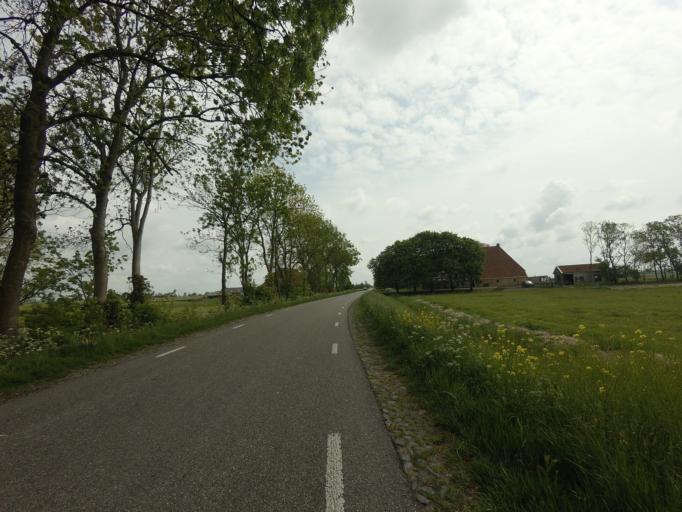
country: NL
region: Friesland
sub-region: Sudwest Fryslan
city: Bolsward
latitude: 53.0992
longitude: 5.5221
